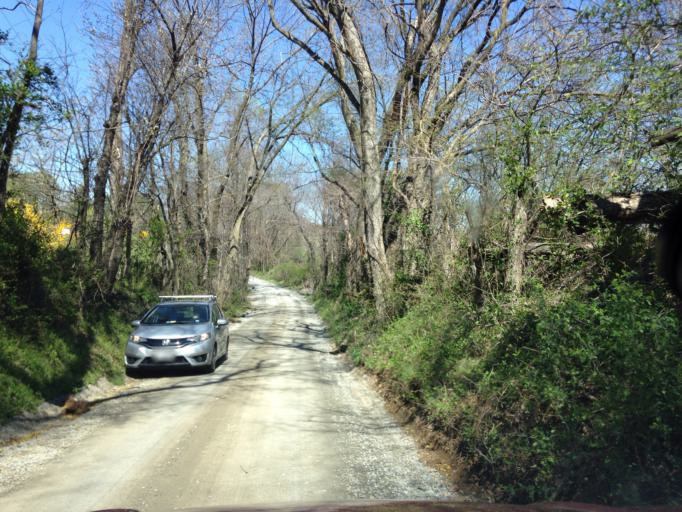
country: US
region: Maryland
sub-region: Frederick County
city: Brunswick
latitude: 39.2895
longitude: -77.5966
